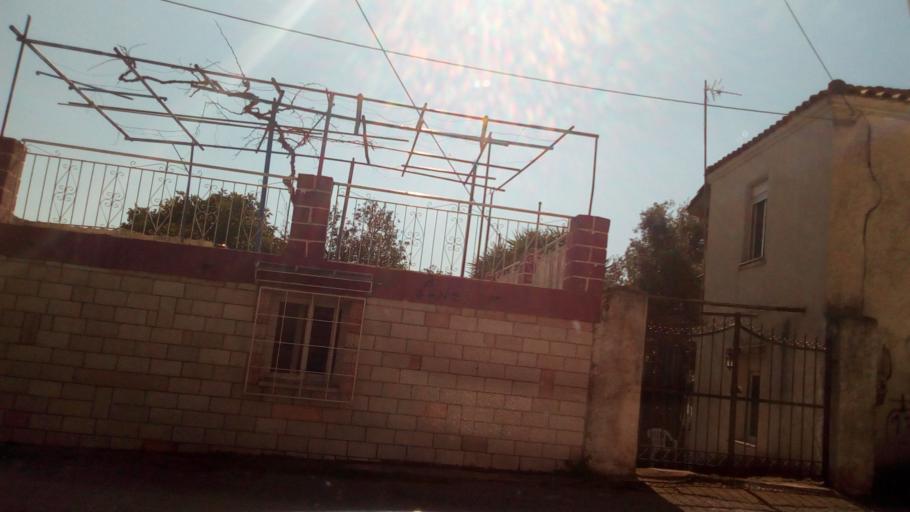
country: GR
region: West Greece
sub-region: Nomos Aitolias kai Akarnanias
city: Nafpaktos
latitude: 38.3948
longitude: 21.8450
